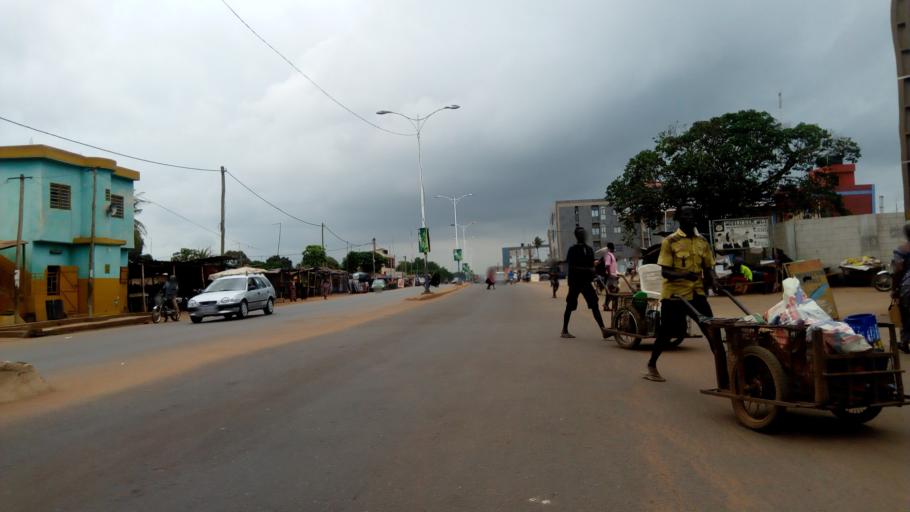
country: TG
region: Maritime
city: Lome
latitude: 6.2276
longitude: 1.2110
